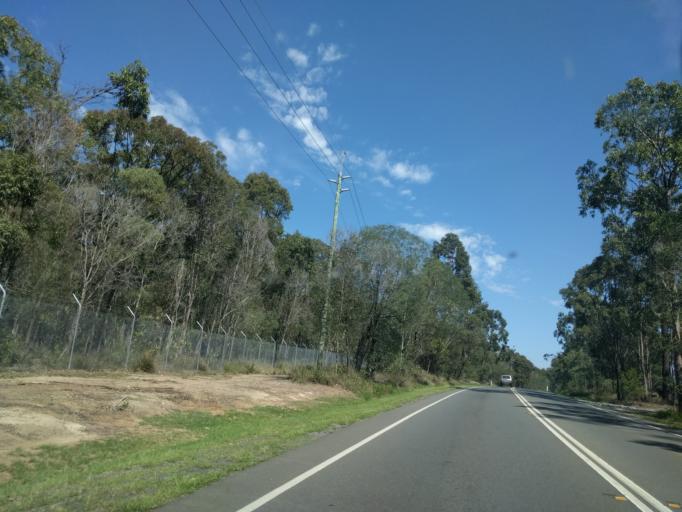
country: AU
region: Queensland
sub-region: Brisbane
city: Forest Lake
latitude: -27.6469
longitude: 152.9797
